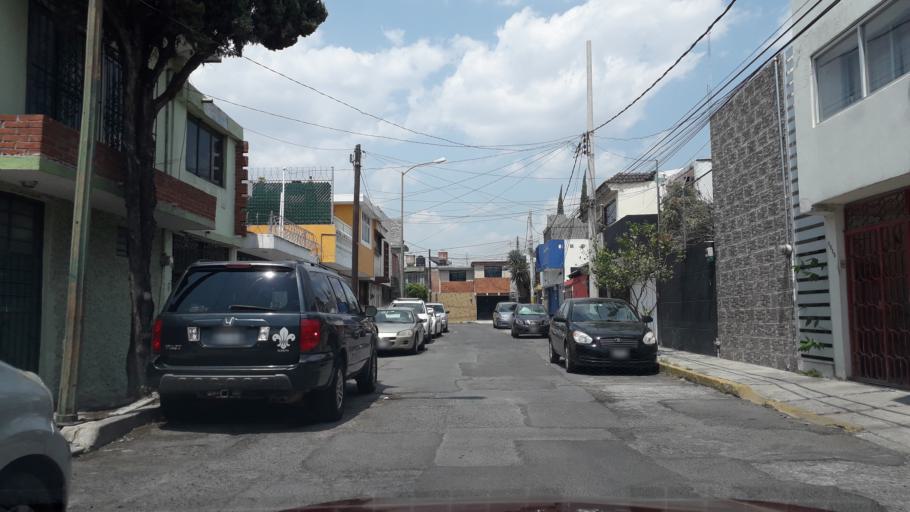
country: MX
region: Puebla
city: Puebla
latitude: 19.0328
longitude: -98.2217
